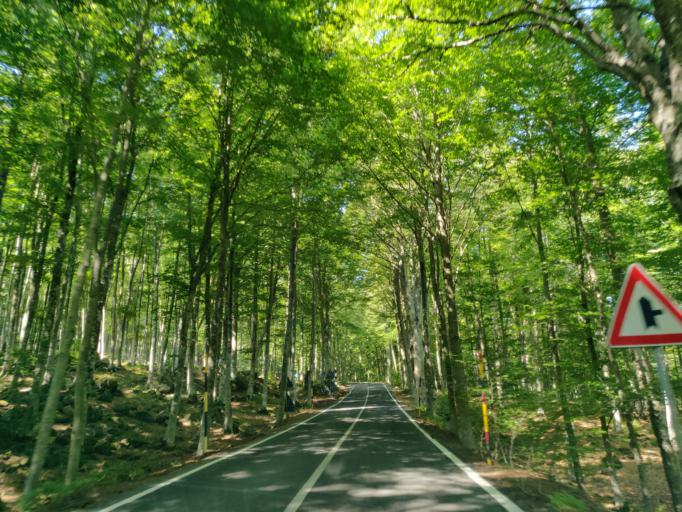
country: IT
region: Tuscany
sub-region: Provincia di Siena
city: Abbadia San Salvatore
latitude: 42.9023
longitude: 11.6277
